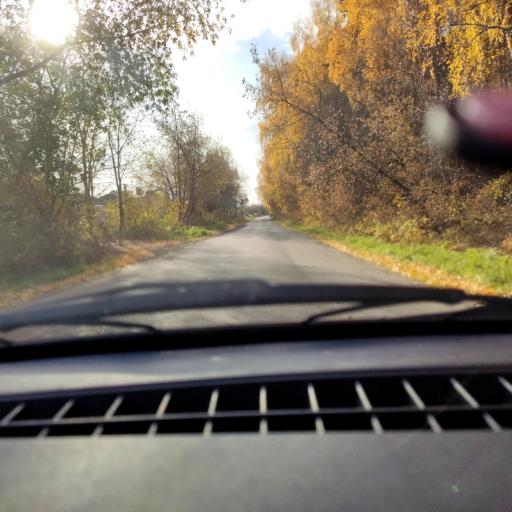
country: RU
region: Bashkortostan
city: Ufa
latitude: 54.7910
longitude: 56.1573
